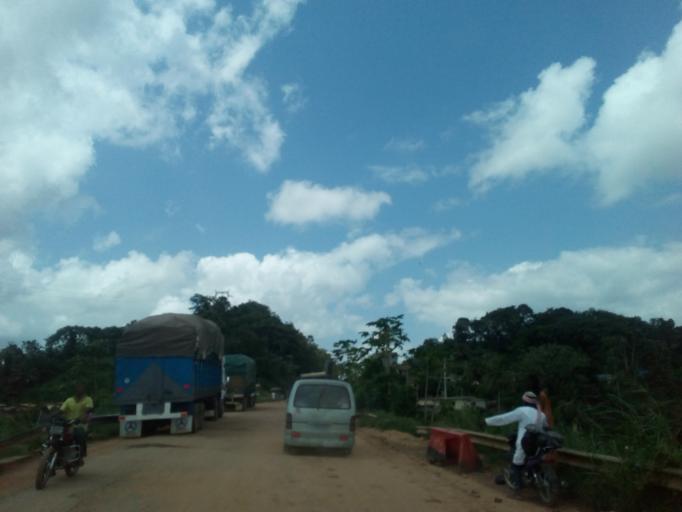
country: CI
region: Sud-Comoe
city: Mafere
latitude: 5.2907
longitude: -2.7917
